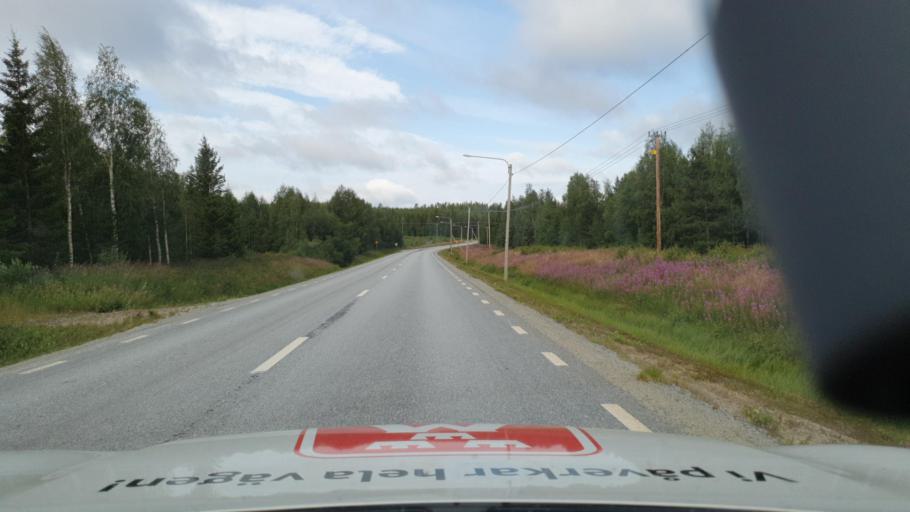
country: SE
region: Vaesterbotten
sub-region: Lycksele Kommun
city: Lycksele
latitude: 64.0696
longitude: 18.4060
